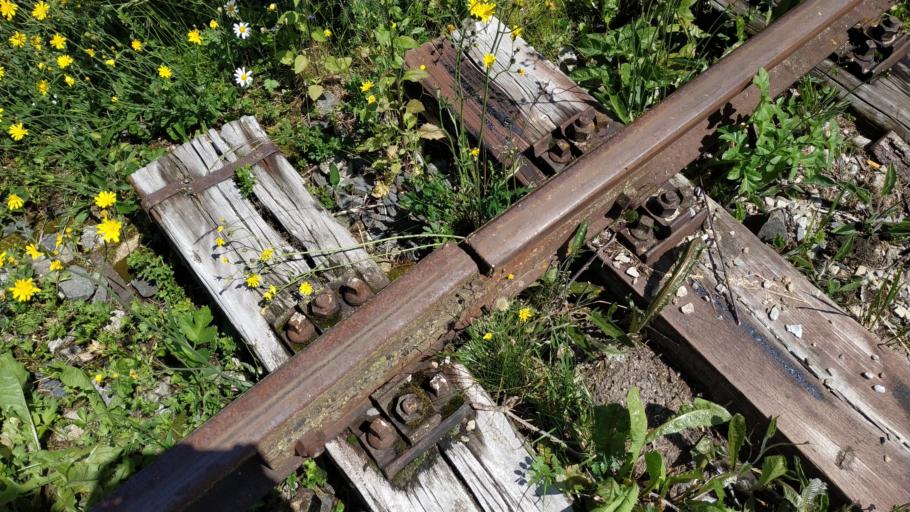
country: DE
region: Bavaria
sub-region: Lower Bavaria
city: Haidmuhle
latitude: 48.8287
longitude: 13.7927
